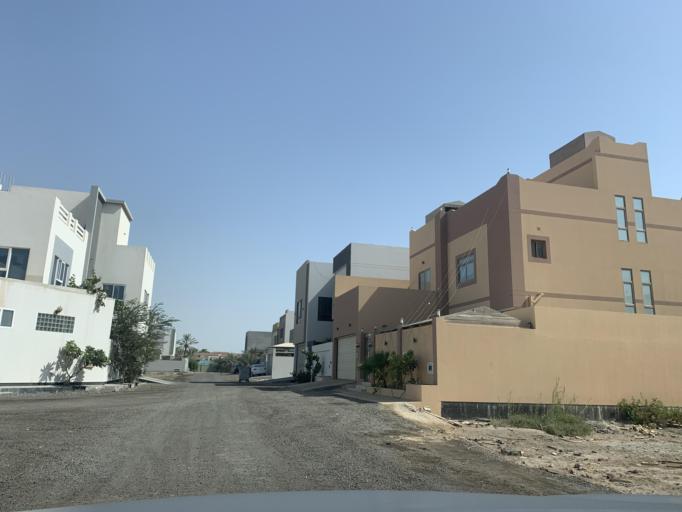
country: BH
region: Manama
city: Jidd Hafs
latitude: 26.2309
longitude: 50.4671
